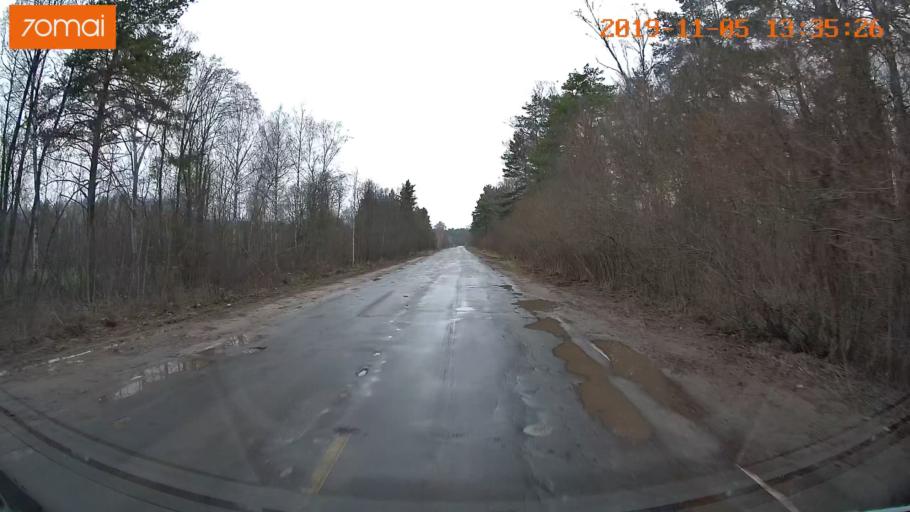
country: RU
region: Ivanovo
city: Shuya
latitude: 56.9078
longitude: 41.3874
